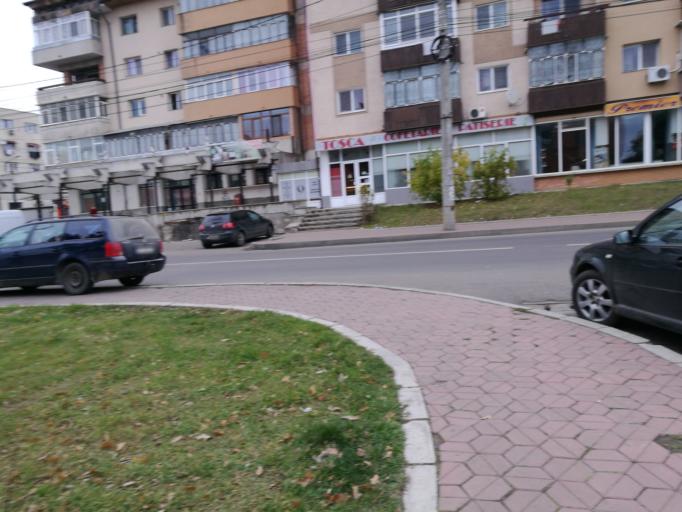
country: RO
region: Suceava
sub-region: Comuna Scheia
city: Scheia
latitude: 47.6708
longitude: 26.2673
